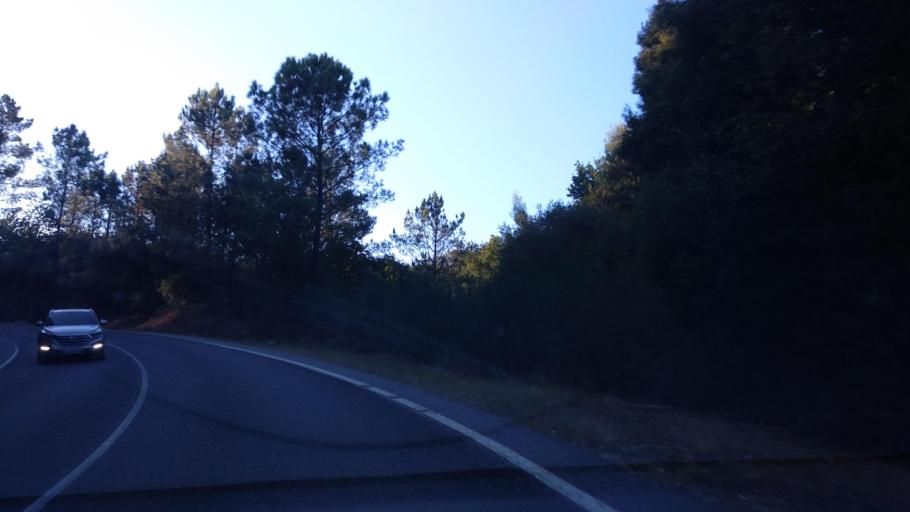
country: ES
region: Galicia
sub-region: Provincia de Pontevedra
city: Ponte Caldelas
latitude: 42.3428
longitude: -8.5577
